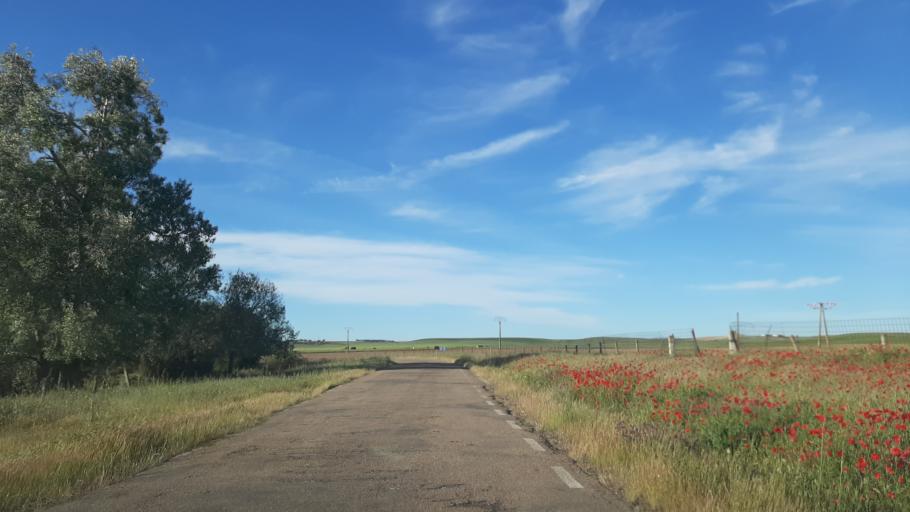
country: ES
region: Castille and Leon
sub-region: Provincia de Salamanca
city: Gajates
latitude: 40.7944
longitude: -5.3728
